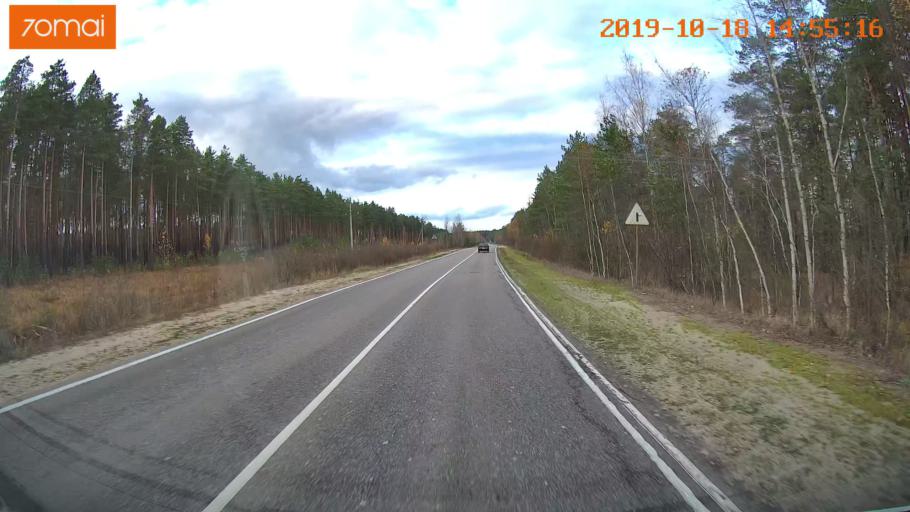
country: RU
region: Vladimir
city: Kurlovo
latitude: 55.4497
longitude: 40.5885
